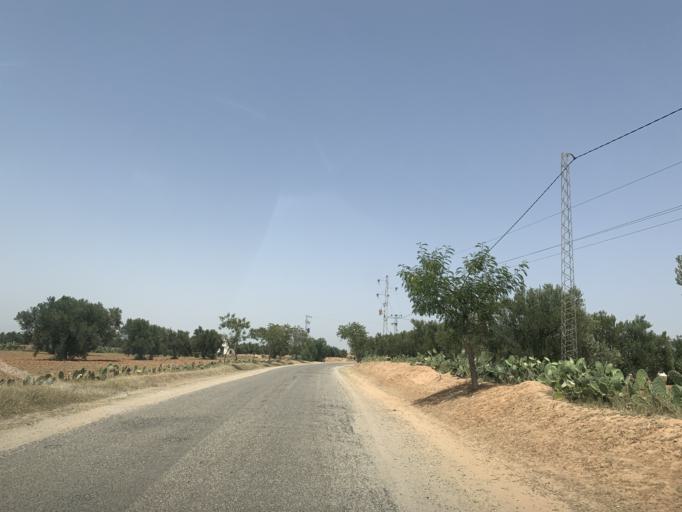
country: TN
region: Al Mahdiyah
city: Shurban
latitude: 35.1872
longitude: 10.2435
